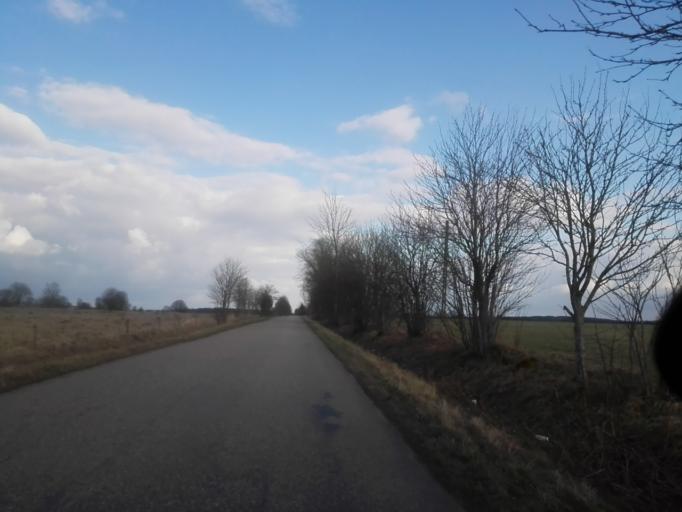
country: PL
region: Podlasie
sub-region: Suwalki
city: Suwalki
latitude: 54.2200
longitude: 22.8438
